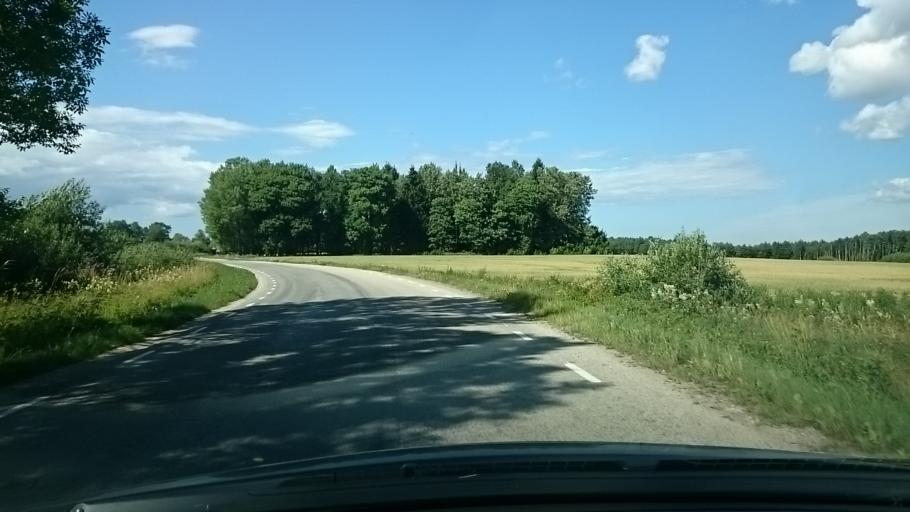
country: EE
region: Laeaene
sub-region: Haapsalu linn
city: Haapsalu
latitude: 59.0330
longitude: 23.5142
